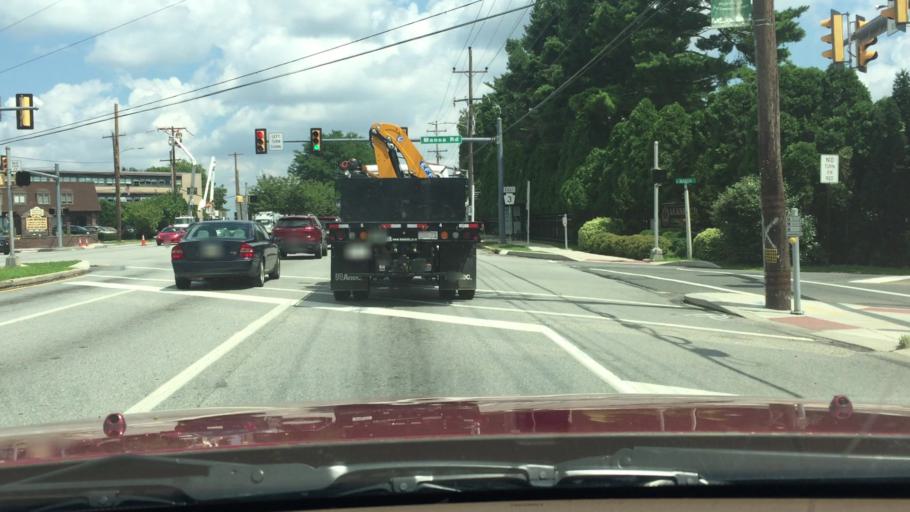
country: US
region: Pennsylvania
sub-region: Delaware County
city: Drexel Hill
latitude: 39.9719
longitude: -75.3138
